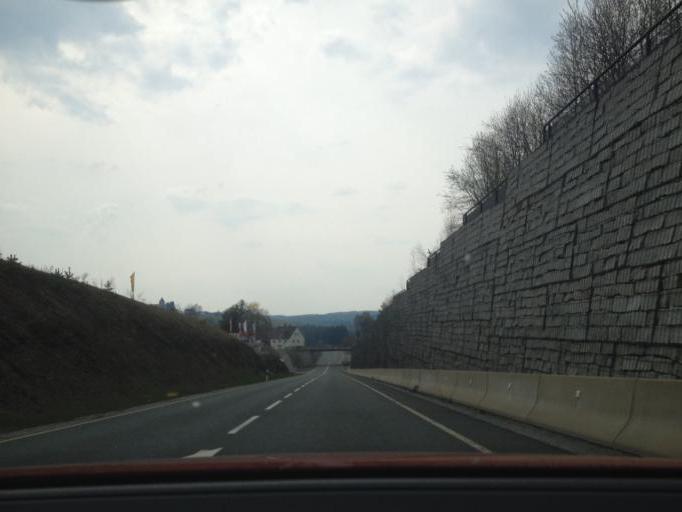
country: DE
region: Bavaria
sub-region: Upper Franconia
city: Bischofsgrun
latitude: 50.0567
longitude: 11.8085
